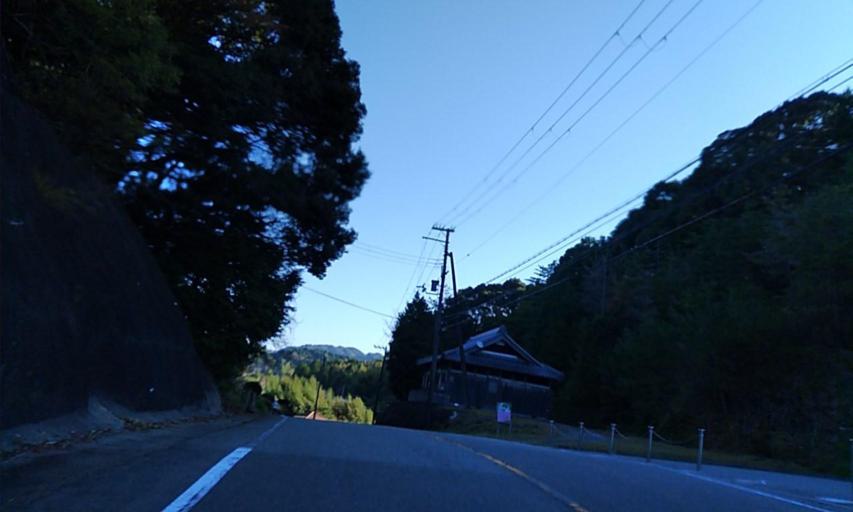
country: JP
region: Wakayama
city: Kainan
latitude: 34.1564
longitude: 135.2940
